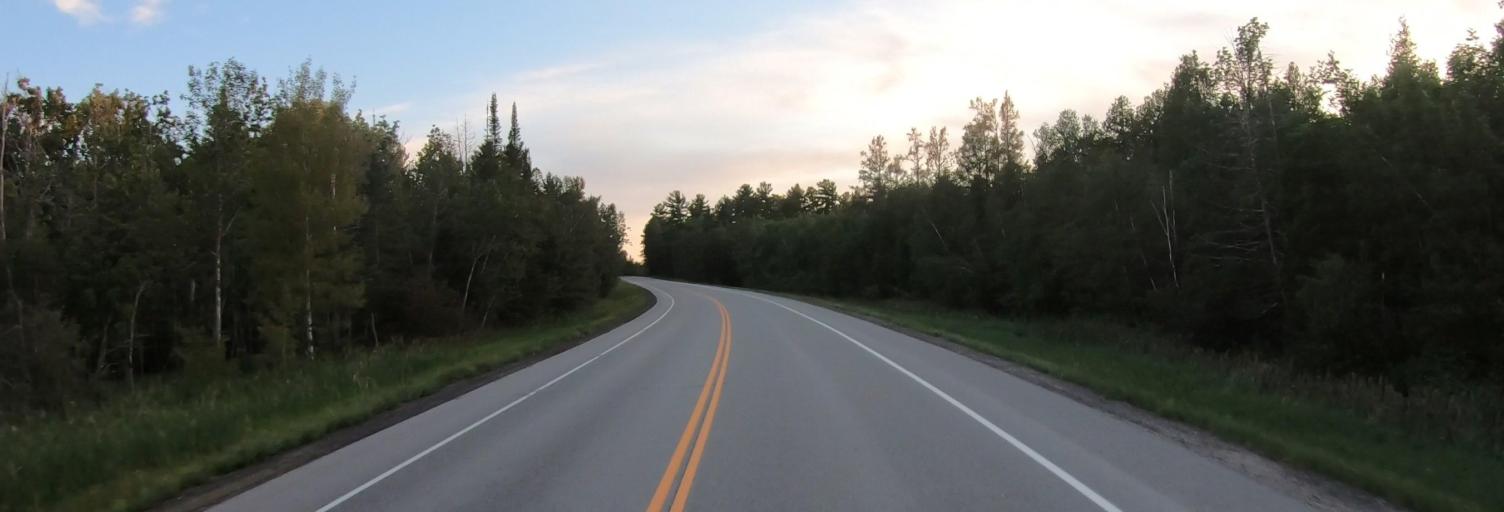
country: US
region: Minnesota
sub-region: Saint Louis County
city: Aurora
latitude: 47.8109
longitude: -92.2538
